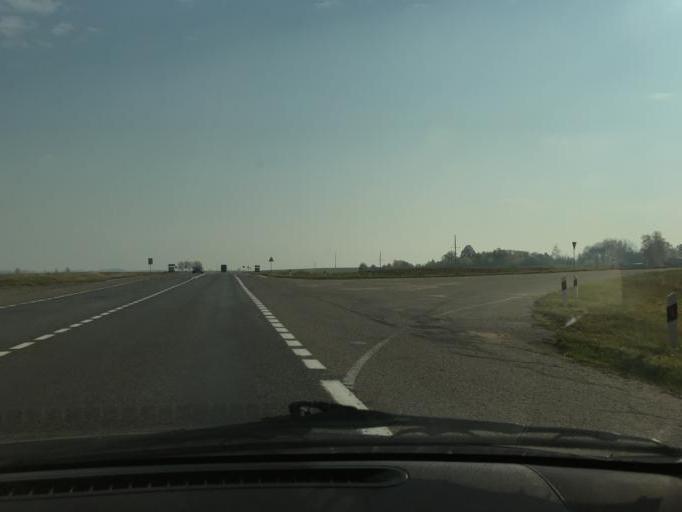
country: BY
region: Vitebsk
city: Chashniki
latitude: 55.0161
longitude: 29.0451
